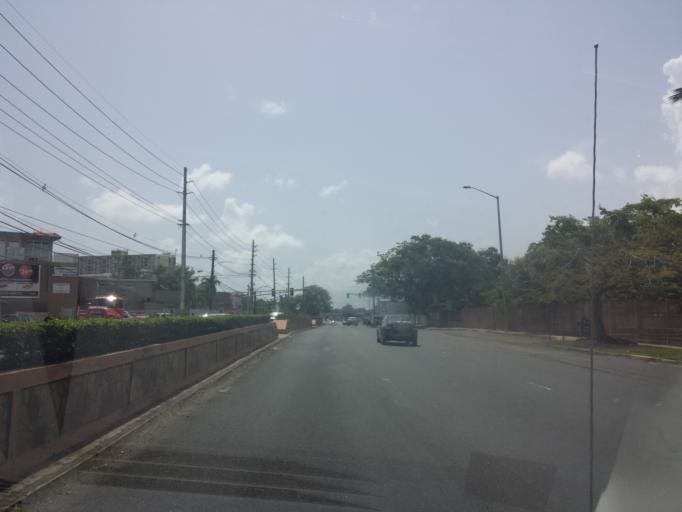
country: PR
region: Bayamon
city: Bayamon
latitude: 18.3957
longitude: -66.1500
